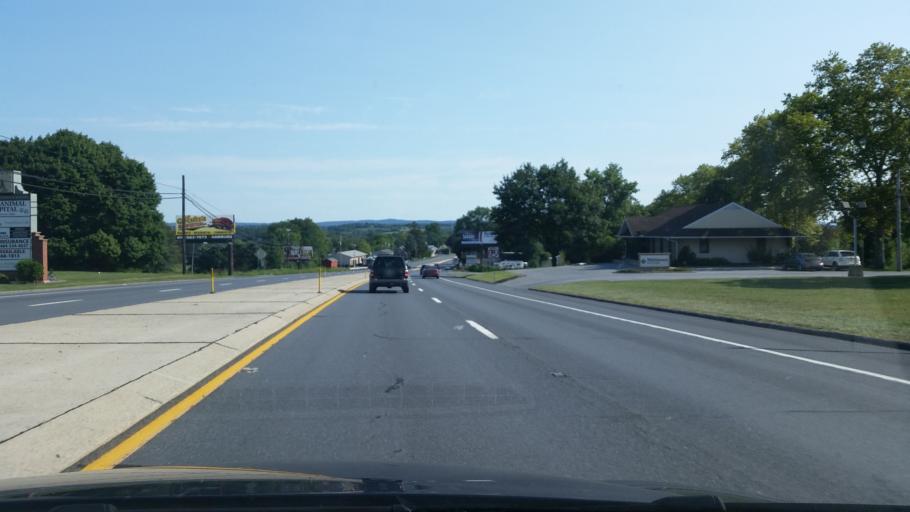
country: US
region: Pennsylvania
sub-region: Berks County
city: Shoemakersville
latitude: 40.5222
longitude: -75.9712
